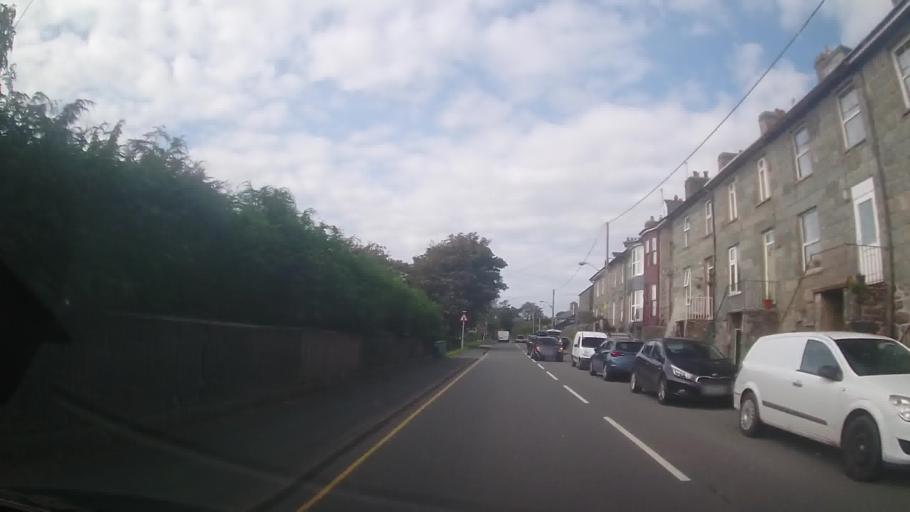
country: GB
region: Wales
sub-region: Gwynedd
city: Llanbedr
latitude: 52.7887
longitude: -4.0970
